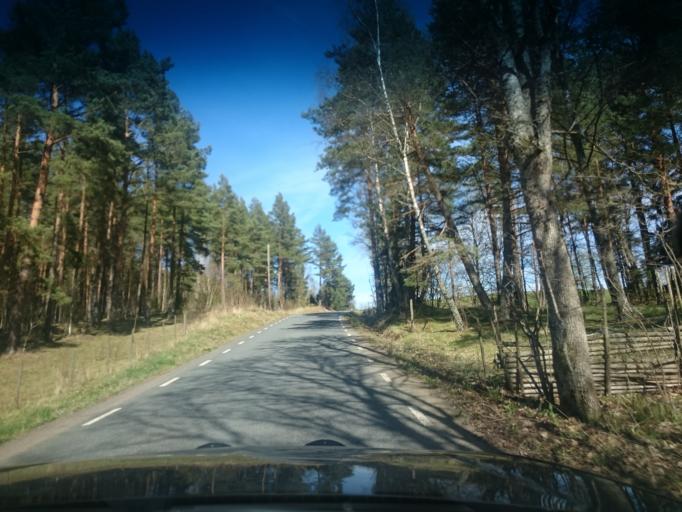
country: SE
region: Kalmar
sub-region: Hultsfreds Kommun
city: Virserum
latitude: 57.3795
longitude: 15.3902
